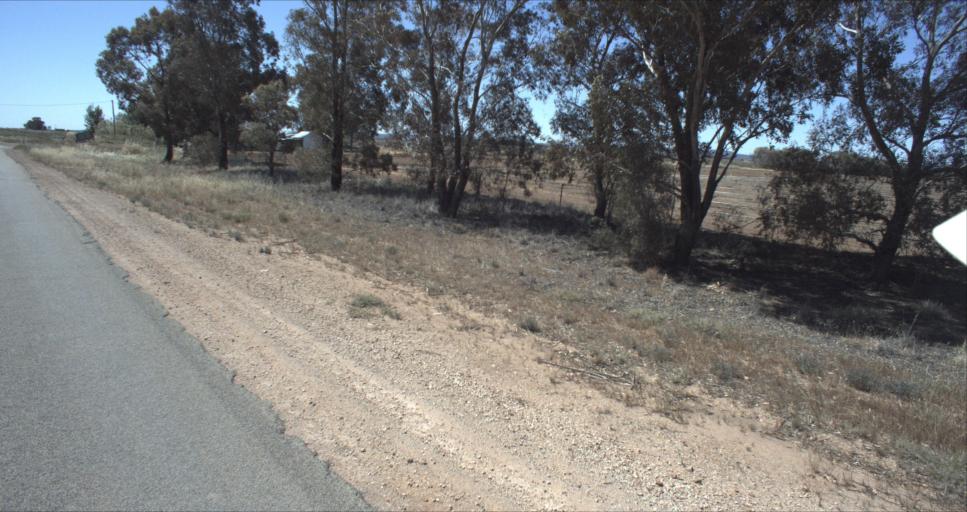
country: AU
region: New South Wales
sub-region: Leeton
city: Leeton
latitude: -34.5122
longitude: 146.3449
